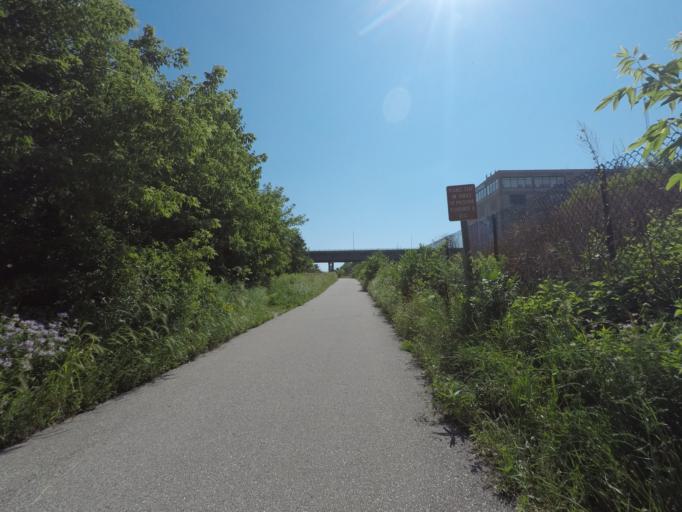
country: US
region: Wisconsin
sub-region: Milwaukee County
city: West Milwaukee
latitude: 43.0243
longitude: -87.9598
